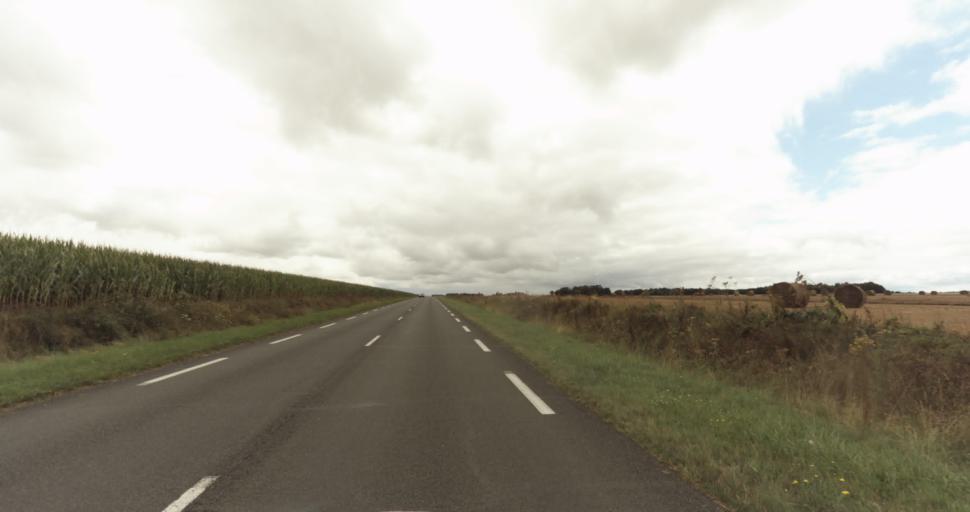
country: FR
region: Haute-Normandie
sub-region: Departement de l'Eure
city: Evreux
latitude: 48.9500
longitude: 1.1627
